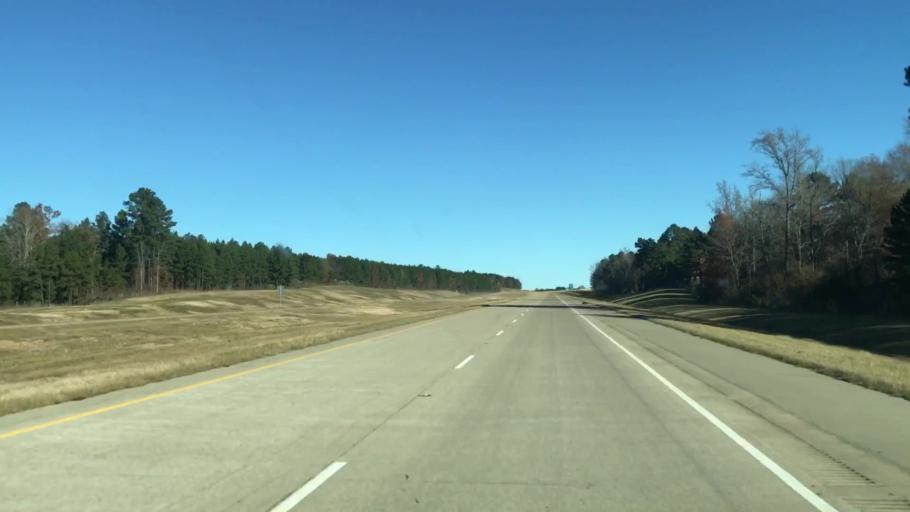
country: US
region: Louisiana
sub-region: Caddo Parish
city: Oil City
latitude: 32.8025
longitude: -93.8857
